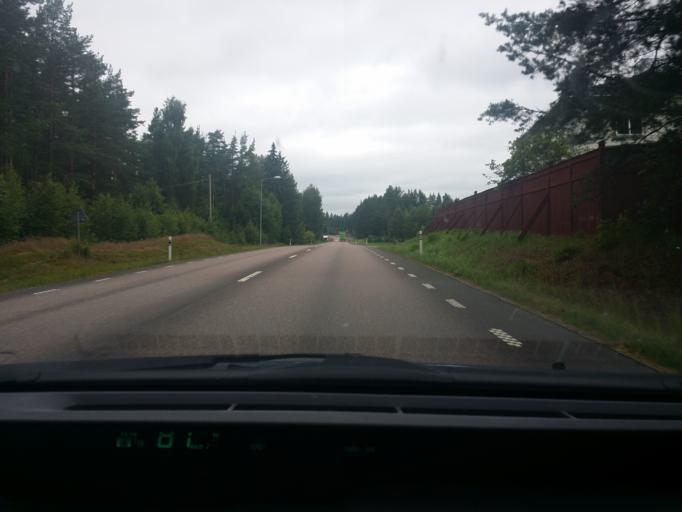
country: SE
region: Dalarna
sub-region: Borlange Kommun
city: Borlaenge
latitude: 60.5246
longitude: 15.3541
